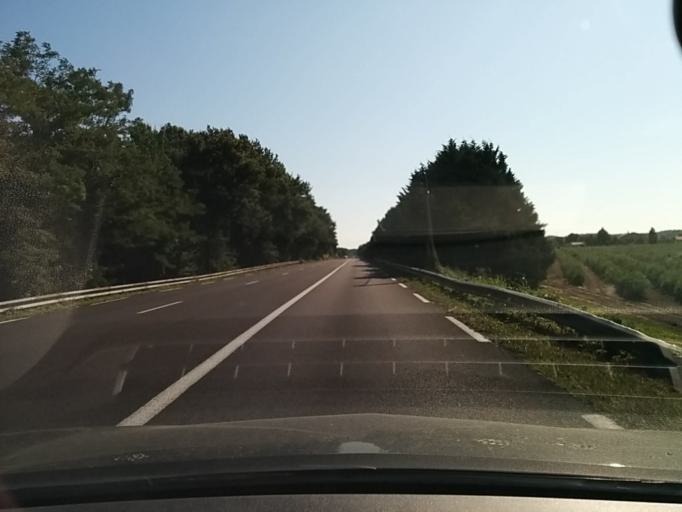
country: FR
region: Aquitaine
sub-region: Departement des Landes
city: Benesse-Maremne
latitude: 43.6242
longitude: -1.3797
